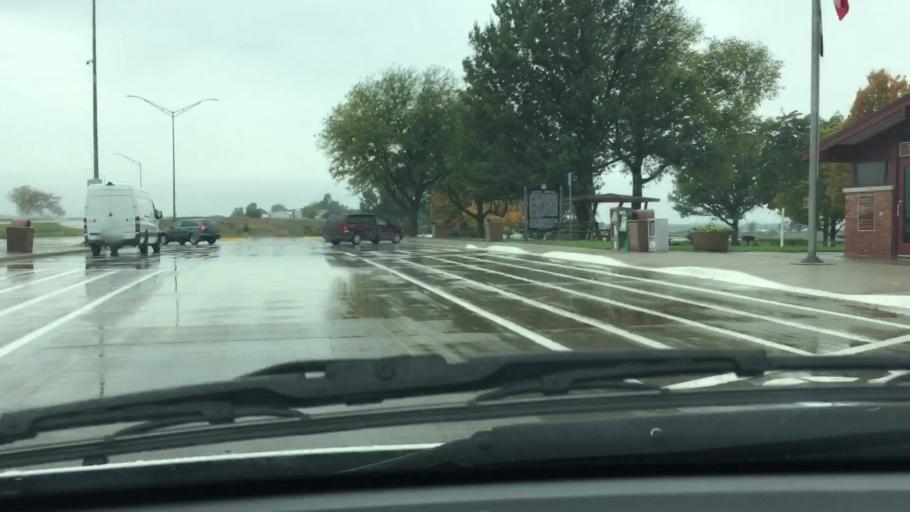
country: US
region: Iowa
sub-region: Iowa County
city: Marengo
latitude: 41.6965
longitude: -92.2317
